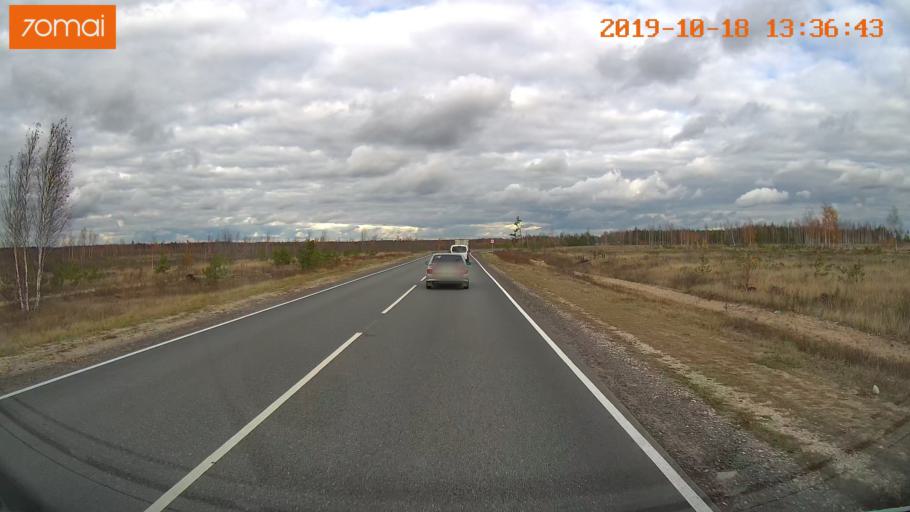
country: RU
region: Rjazan
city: Solotcha
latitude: 54.8734
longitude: 39.9869
